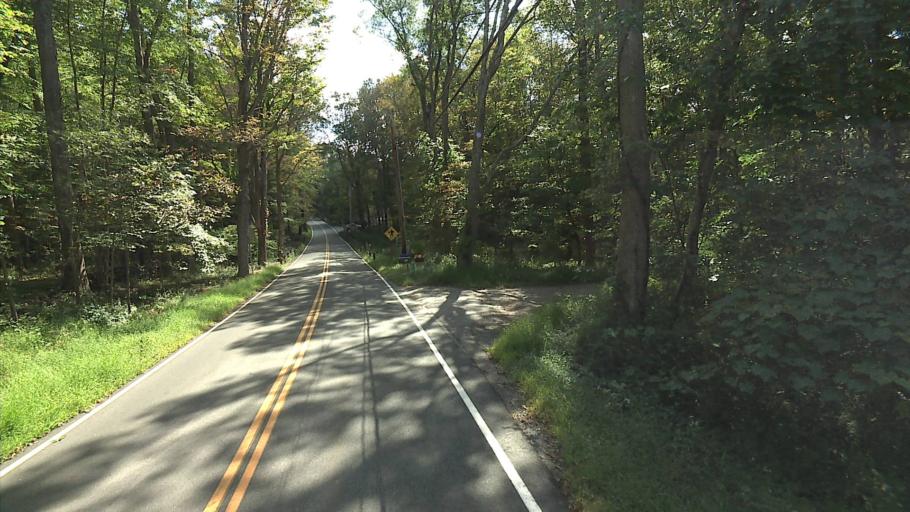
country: US
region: Connecticut
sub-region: Middlesex County
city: East Haddam
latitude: 41.4377
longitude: -72.4347
